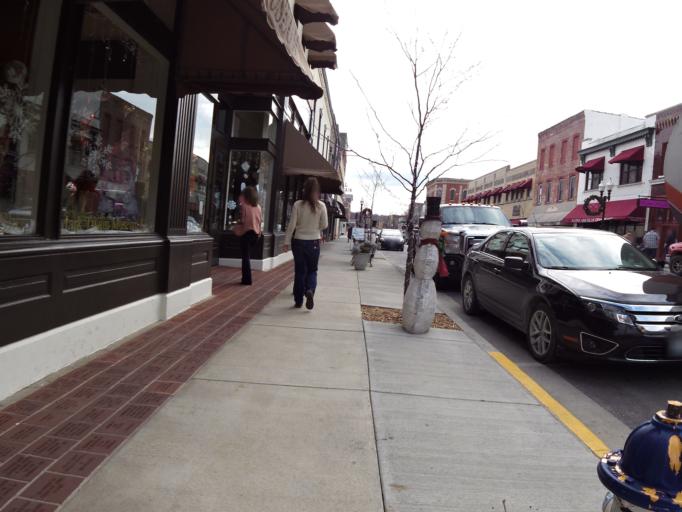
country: US
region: Missouri
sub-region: Marion County
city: Hannibal
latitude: 39.7105
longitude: -91.3563
